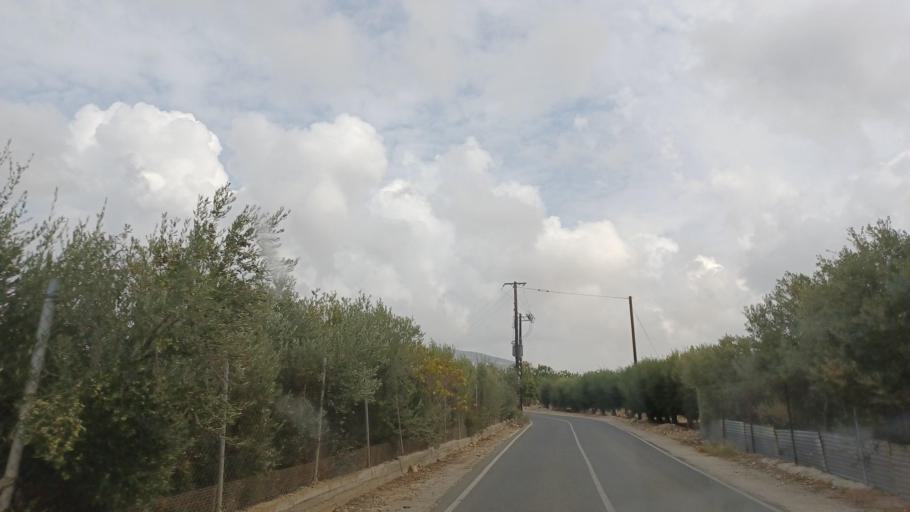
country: CY
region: Pafos
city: Kissonerga
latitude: 34.8297
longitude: 32.4172
